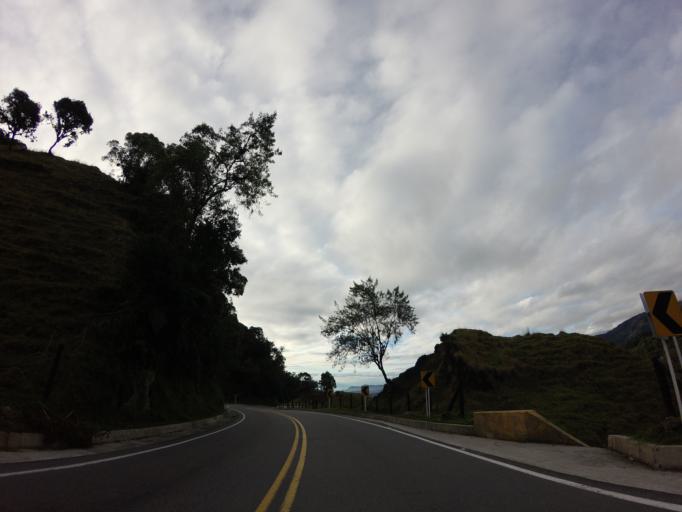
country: CO
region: Tolima
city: Herveo
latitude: 5.1078
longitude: -75.2701
